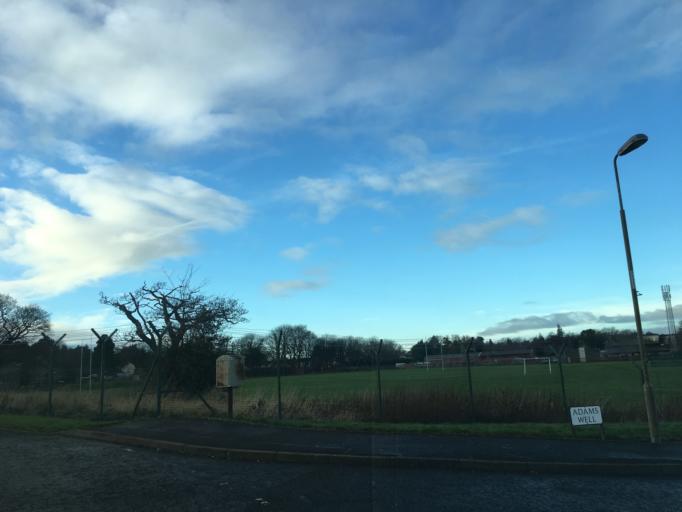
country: GB
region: Scotland
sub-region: Edinburgh
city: Colinton
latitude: 55.9073
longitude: -3.2434
